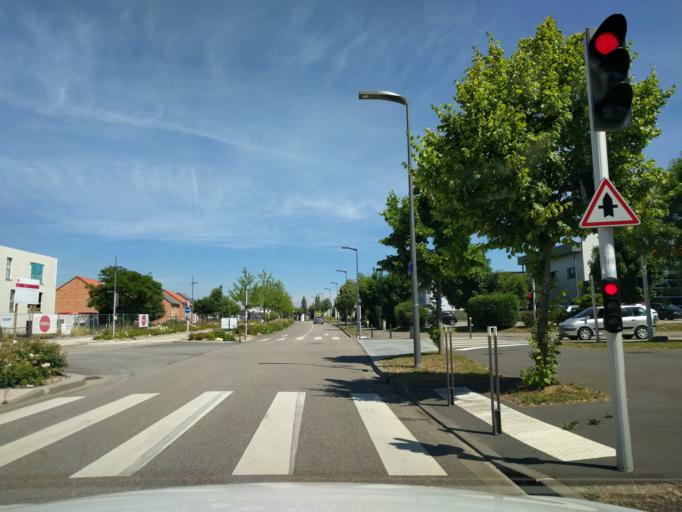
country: FR
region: Lorraine
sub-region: Departement de la Moselle
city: Saint-Julien-les-Metz
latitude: 49.1115
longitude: 6.2307
